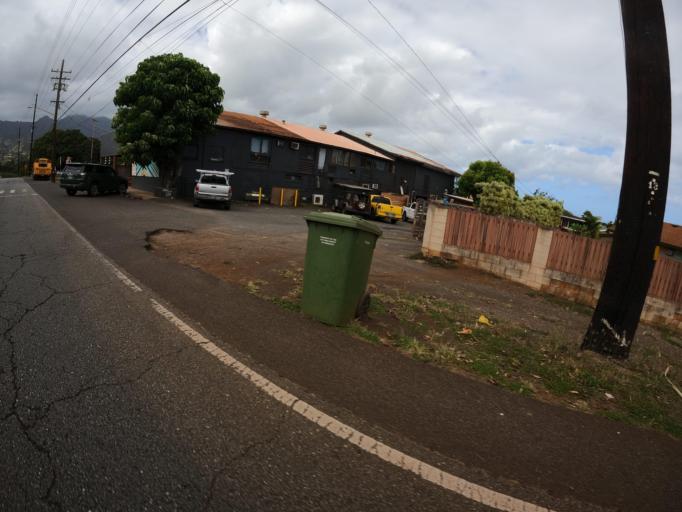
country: US
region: Hawaii
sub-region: Honolulu County
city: Hale'iwa
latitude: 21.5690
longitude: -158.1091
